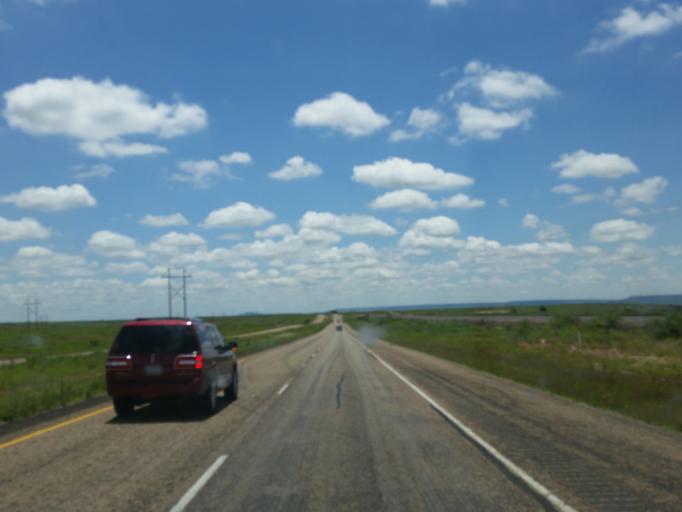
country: US
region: Texas
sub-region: Garza County
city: Post
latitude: 33.1172
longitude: -101.2778
